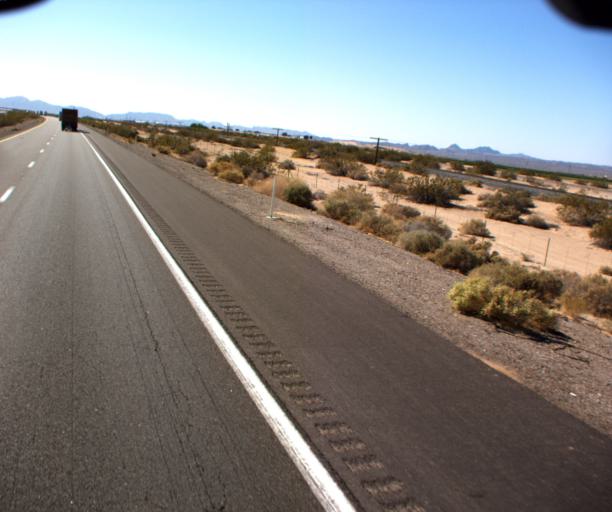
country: US
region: Arizona
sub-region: Yuma County
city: Wellton
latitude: 32.6730
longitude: -114.0920
